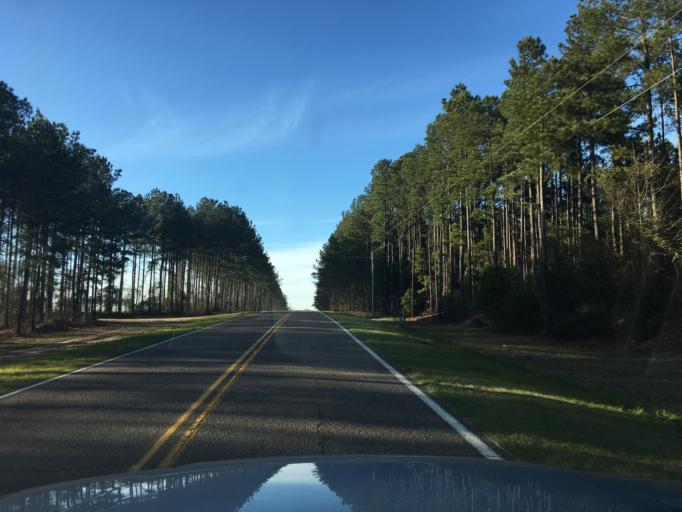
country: US
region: South Carolina
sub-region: Lexington County
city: Batesburg
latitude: 33.8162
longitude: -81.6532
